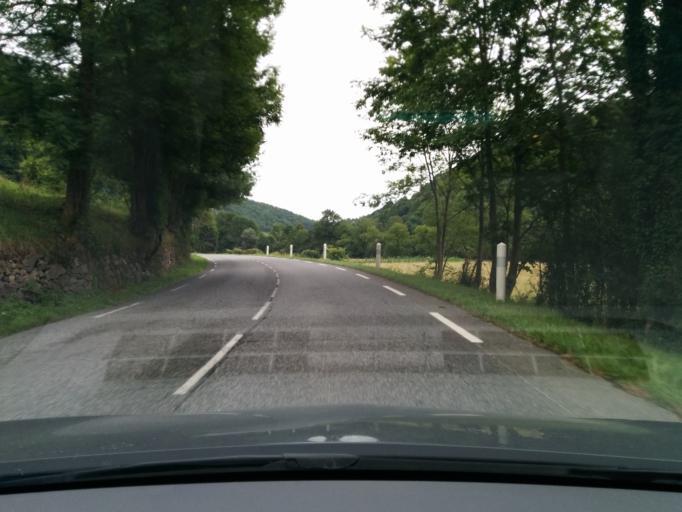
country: FR
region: Midi-Pyrenees
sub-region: Departement des Hautes-Pyrenees
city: La Barthe-de-Neste
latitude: 42.9855
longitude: 0.3760
